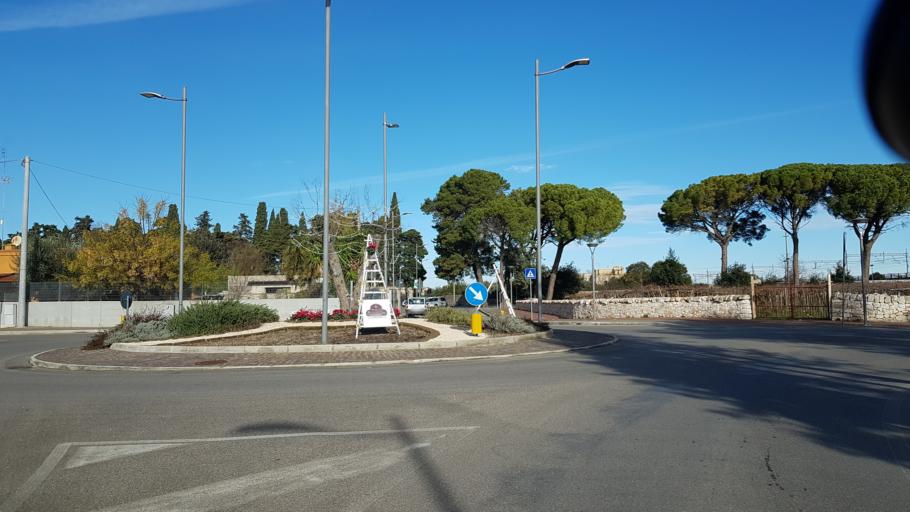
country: IT
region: Apulia
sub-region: Provincia di Bari
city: Gioia del Colle
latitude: 40.8006
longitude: 16.9153
